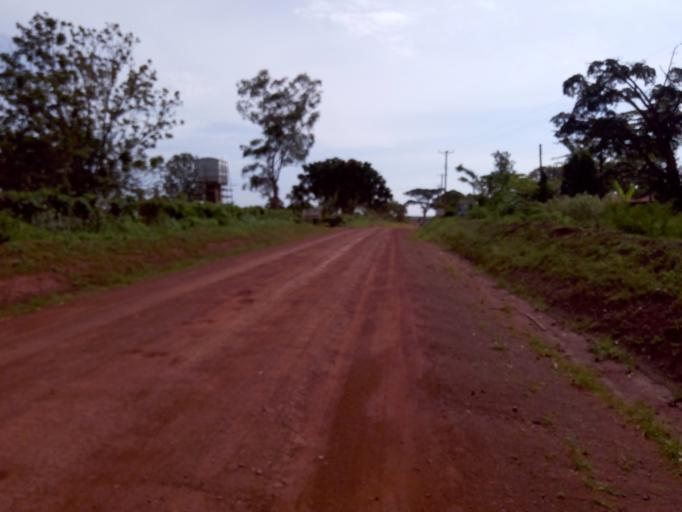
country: UG
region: Western Region
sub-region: Masindi District
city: Masindi
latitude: 1.6934
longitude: 31.7178
